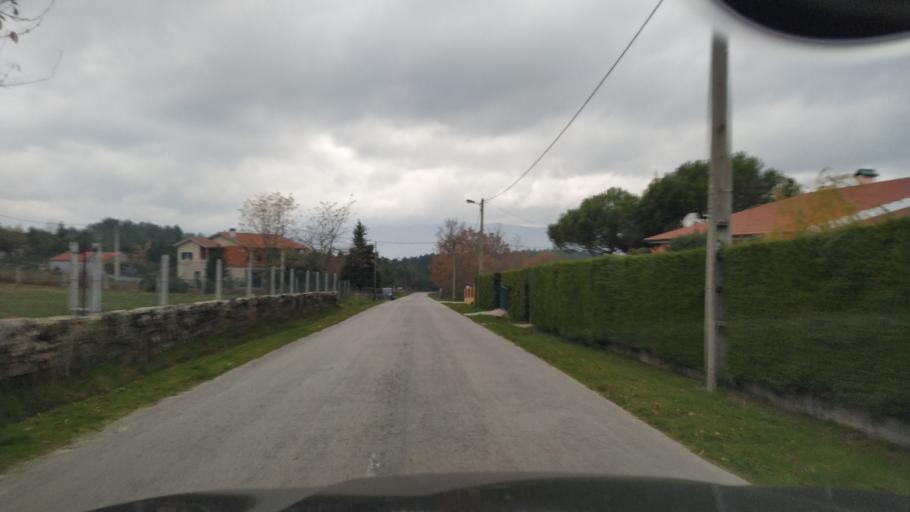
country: PT
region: Vila Real
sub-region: Sabrosa
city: Sabrosa
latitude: 41.3321
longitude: -7.6447
